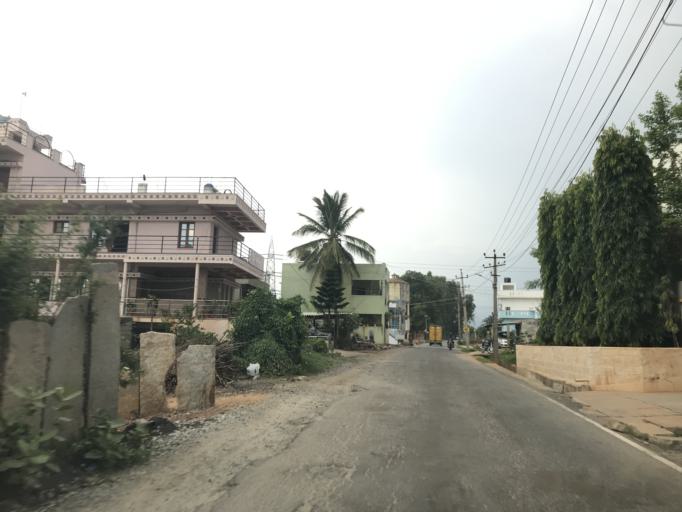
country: IN
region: Karnataka
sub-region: Bangalore Rural
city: Devanhalli
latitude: 13.1776
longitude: 77.6521
